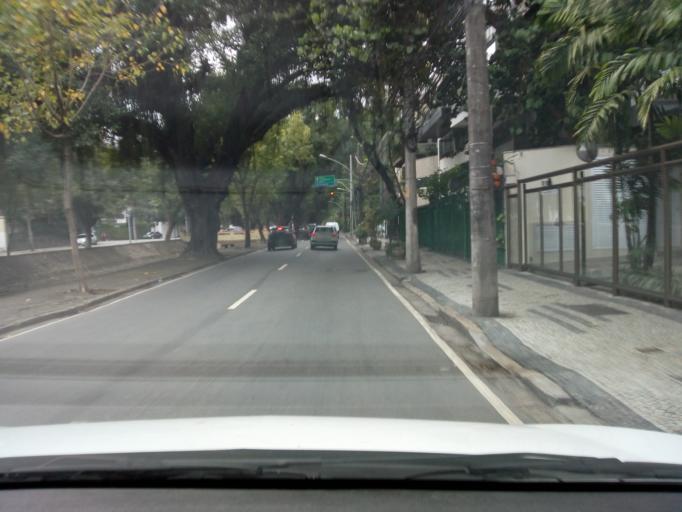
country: BR
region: Rio de Janeiro
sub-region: Rio De Janeiro
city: Rio de Janeiro
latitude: -22.9841
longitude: -43.2287
